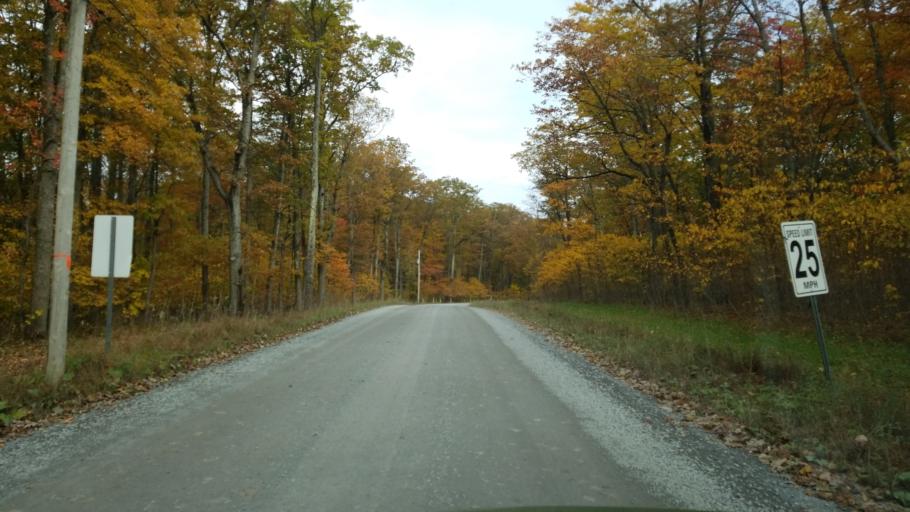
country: US
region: Pennsylvania
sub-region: Clearfield County
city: Clearfield
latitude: 41.1406
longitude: -78.5020
